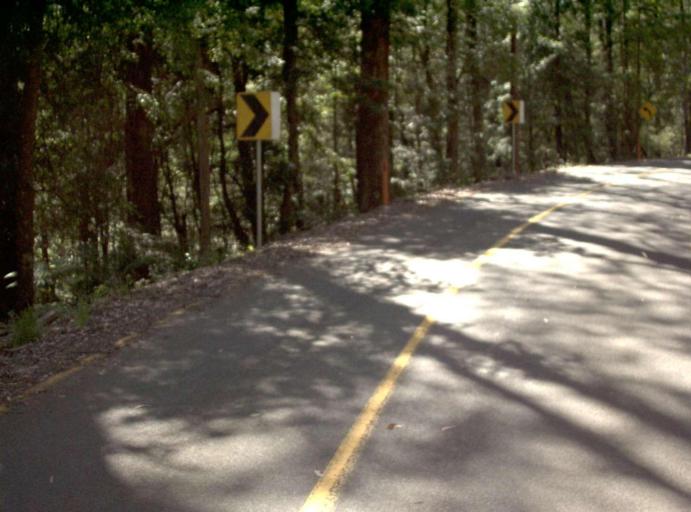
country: AU
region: Victoria
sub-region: Yarra Ranges
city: Millgrove
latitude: -37.5375
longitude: 145.8412
